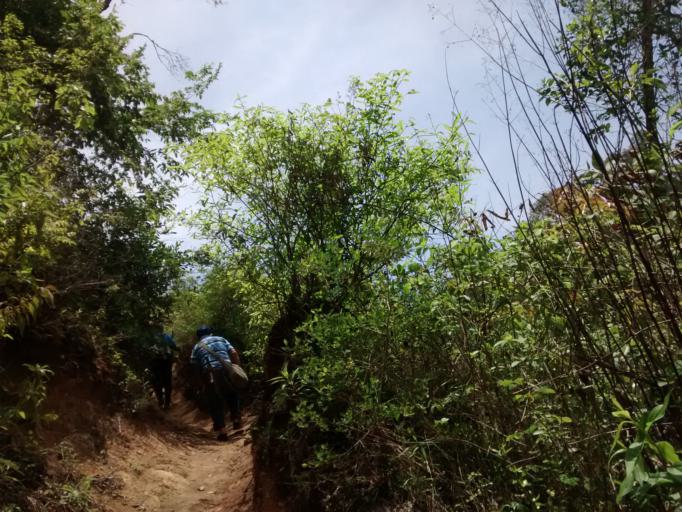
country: GT
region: Sacatepequez
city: Santo Domingo Xenacoj
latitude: 14.6930
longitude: -90.7179
